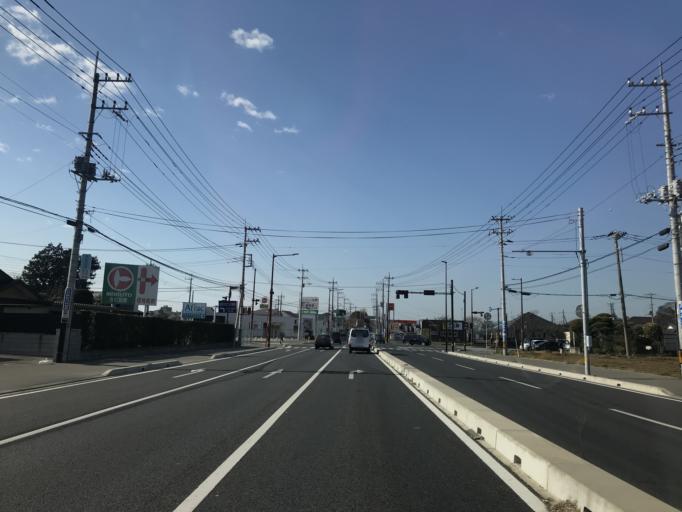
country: JP
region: Ibaraki
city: Mito-shi
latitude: 36.3375
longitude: 140.4619
